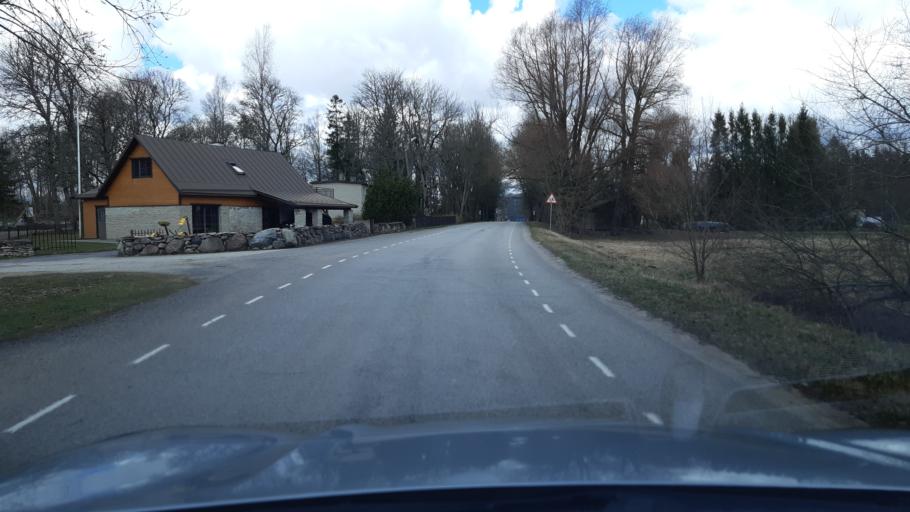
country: EE
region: Raplamaa
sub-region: Kehtna vald
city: Kehtna
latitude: 59.0427
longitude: 25.1193
